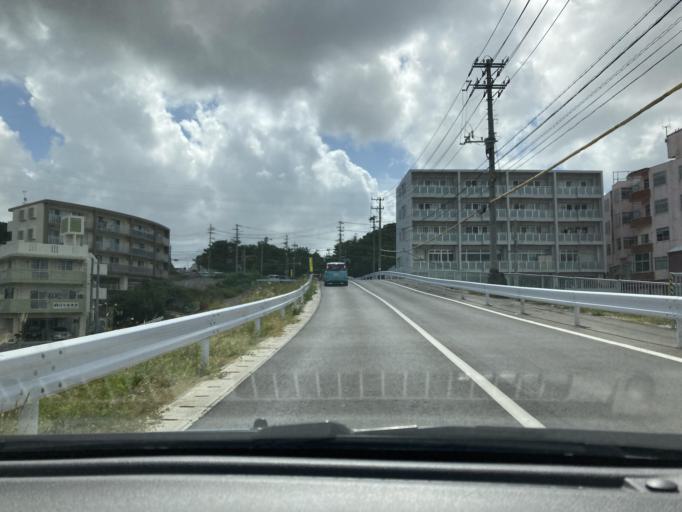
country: JP
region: Okinawa
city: Ginowan
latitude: 26.2584
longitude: 127.7251
